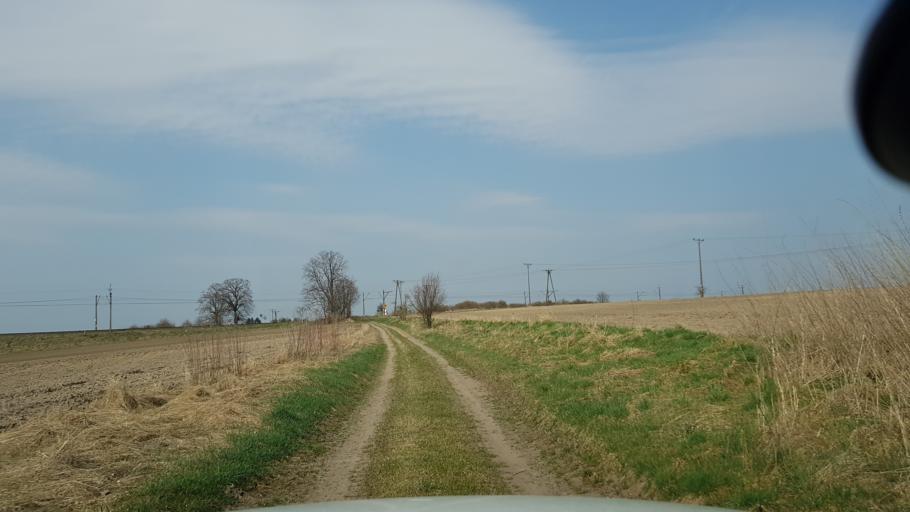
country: PL
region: West Pomeranian Voivodeship
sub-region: Powiat stargardzki
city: Stargard Szczecinski
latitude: 53.3323
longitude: 15.0817
